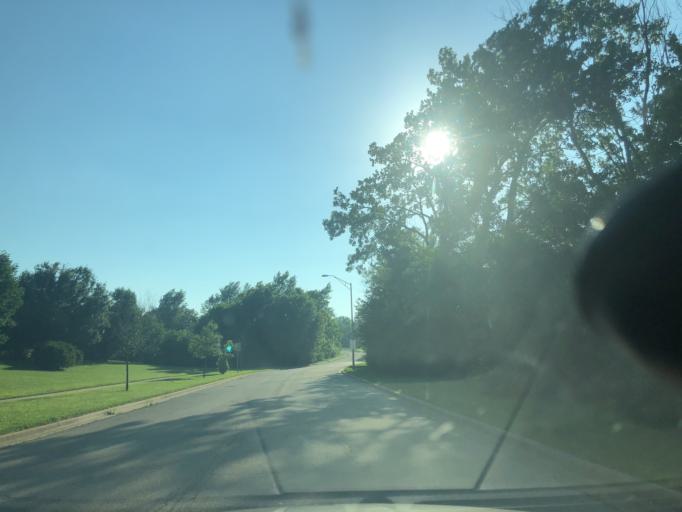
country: US
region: Illinois
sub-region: Will County
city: Mokena
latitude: 41.5568
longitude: -87.9010
